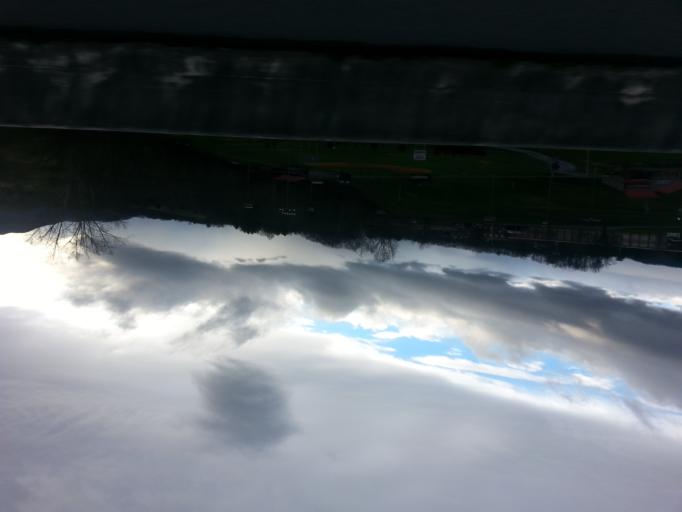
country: US
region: Tennessee
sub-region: Carter County
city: Central
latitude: 36.3186
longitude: -82.2803
